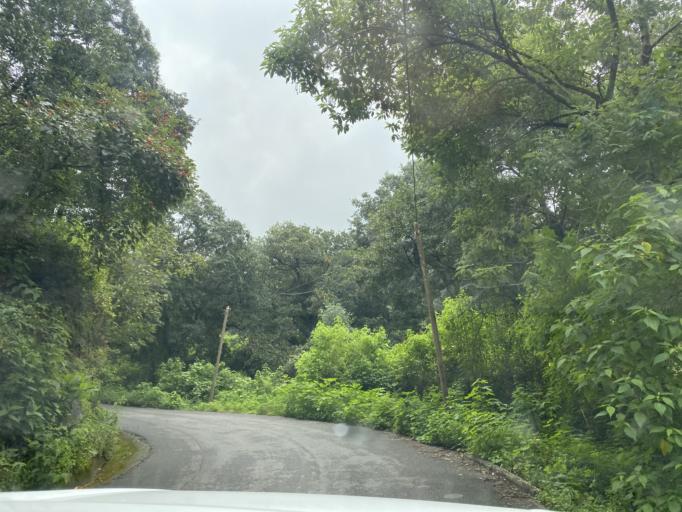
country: MX
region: Morelos
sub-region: Yecapixtla
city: Achichipico
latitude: 18.9389
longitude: -98.8195
